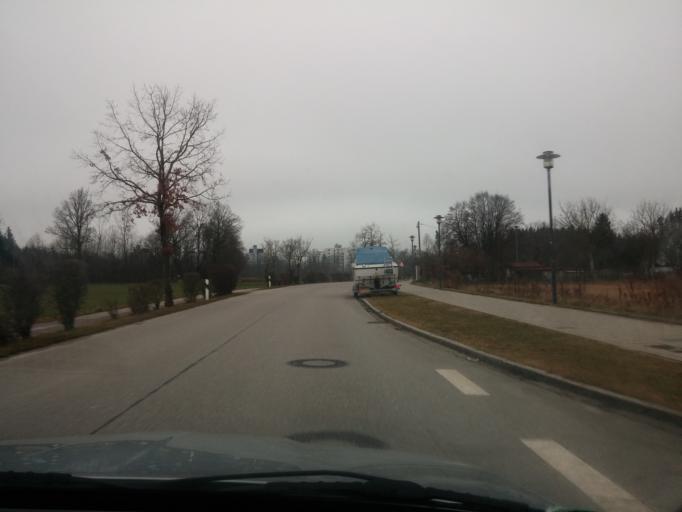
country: DE
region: Bavaria
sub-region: Upper Bavaria
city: Putzbrunn
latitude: 48.0799
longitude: 11.6941
